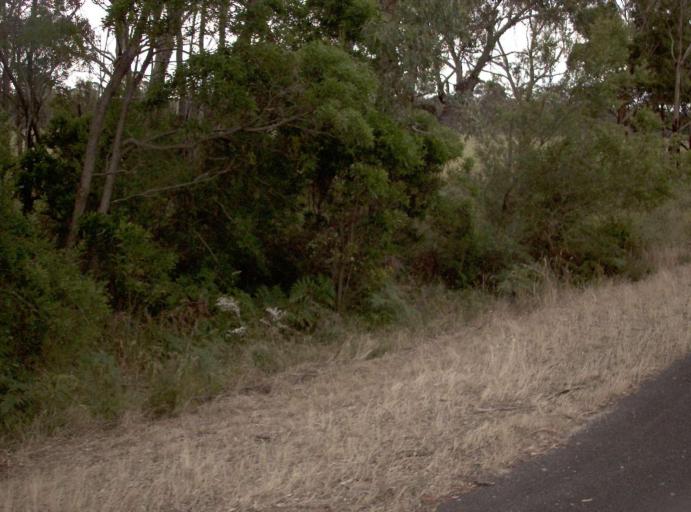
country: AU
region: Victoria
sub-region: Wellington
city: Sale
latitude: -38.4713
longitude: 146.9288
